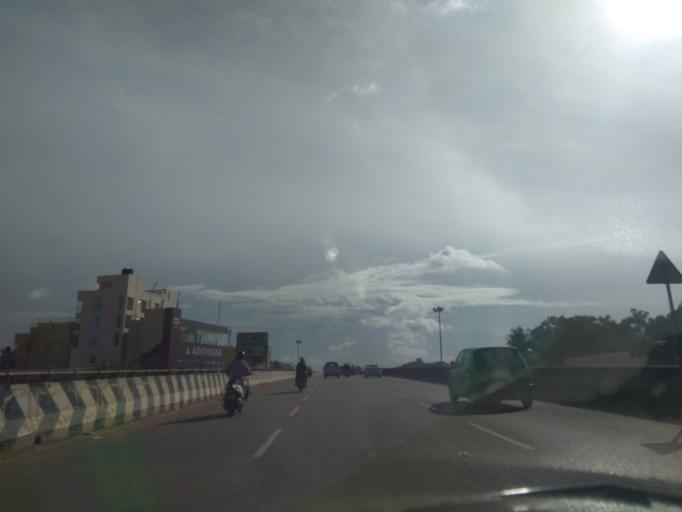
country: IN
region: Karnataka
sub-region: Bangalore Rural
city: Hoskote
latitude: 13.0712
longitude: 77.7852
